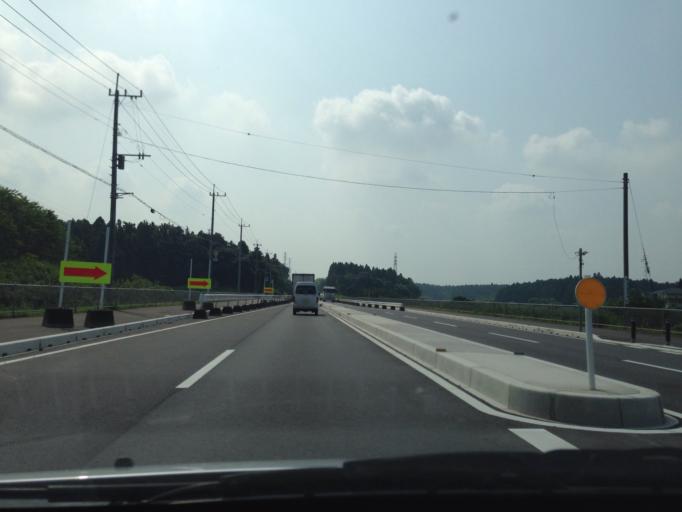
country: JP
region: Ibaraki
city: Ami
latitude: 36.0325
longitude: 140.2267
